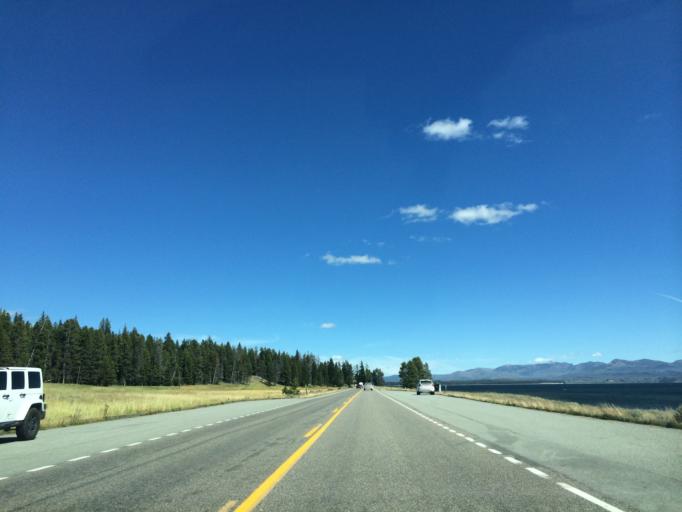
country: US
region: Montana
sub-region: Gallatin County
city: West Yellowstone
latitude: 44.5396
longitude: -110.4276
